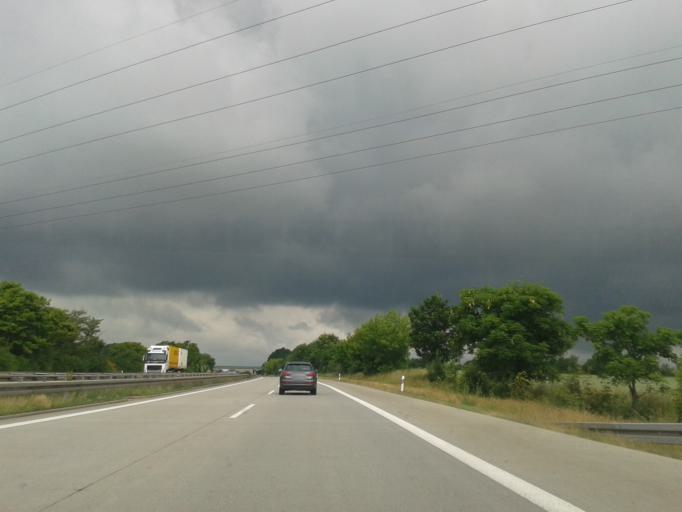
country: DE
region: Saxony
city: Nossen
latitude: 51.0661
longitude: 13.3293
